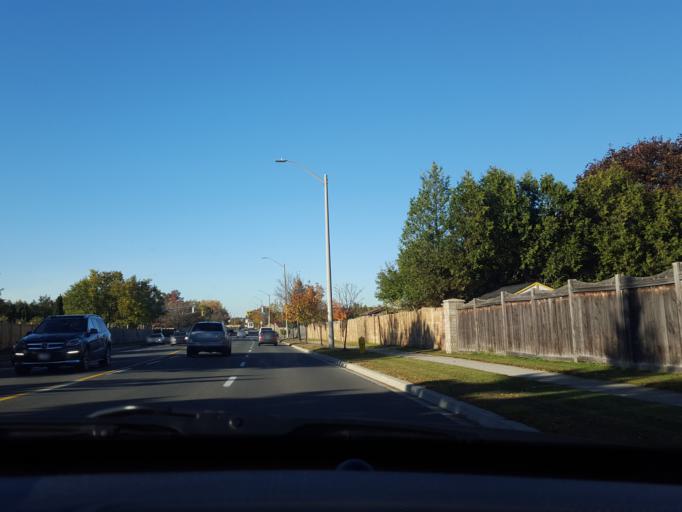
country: CA
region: Ontario
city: Markham
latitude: 43.8354
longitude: -79.2893
